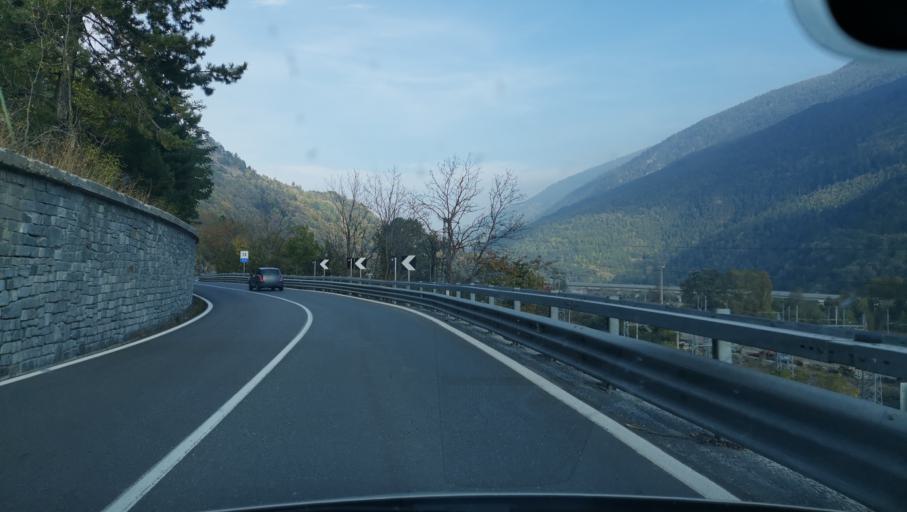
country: IT
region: Piedmont
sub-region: Provincia di Torino
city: Salbertrand
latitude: 45.0748
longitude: 6.8867
